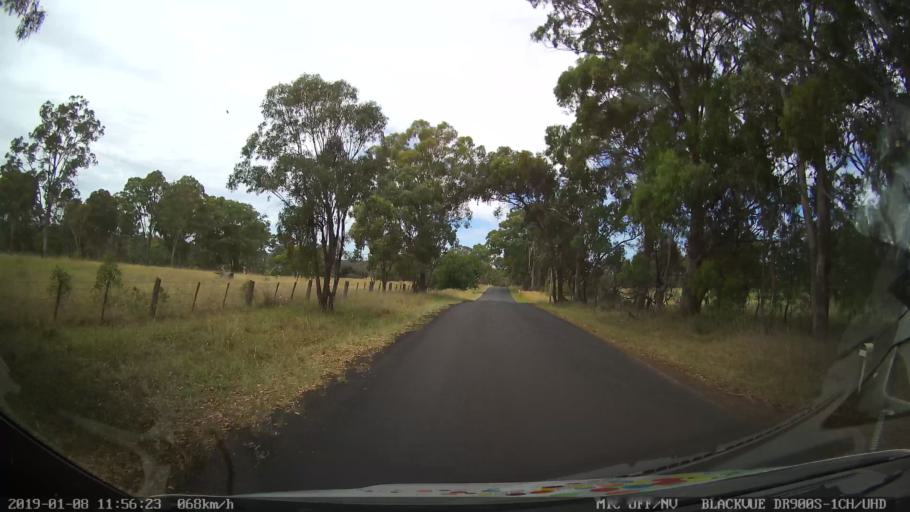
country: AU
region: New South Wales
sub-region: Armidale Dumaresq
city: Armidale
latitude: -30.4394
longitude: 151.5651
